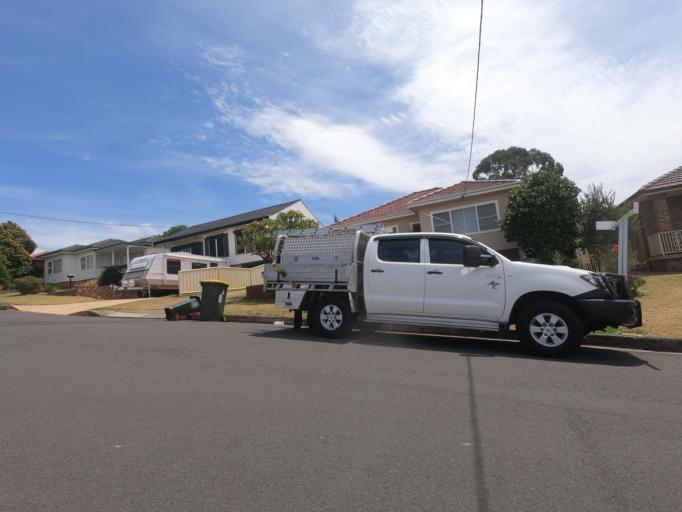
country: AU
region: New South Wales
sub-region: Wollongong
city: Mount Ousley
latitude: -34.3909
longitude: 150.8831
